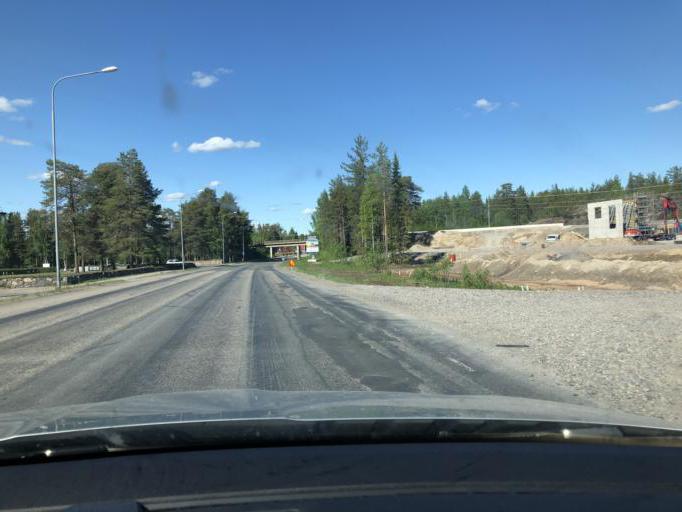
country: SE
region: Norrbotten
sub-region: Kalix Kommun
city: Kalix
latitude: 65.8646
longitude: 23.1397
